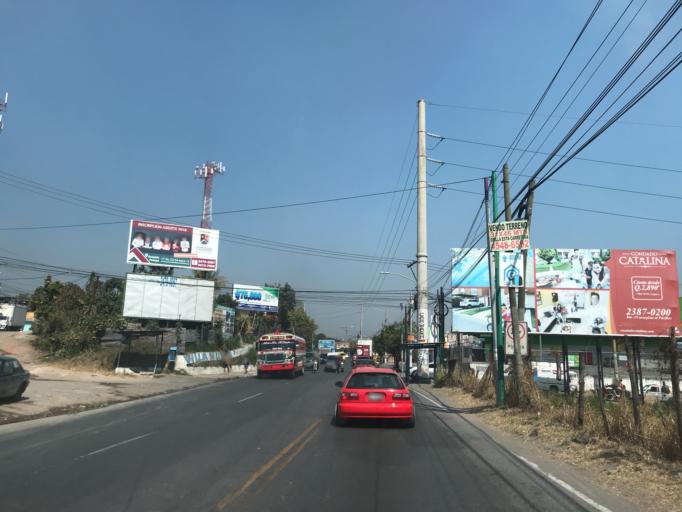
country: GT
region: Guatemala
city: Petapa
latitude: 14.5156
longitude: -90.5639
